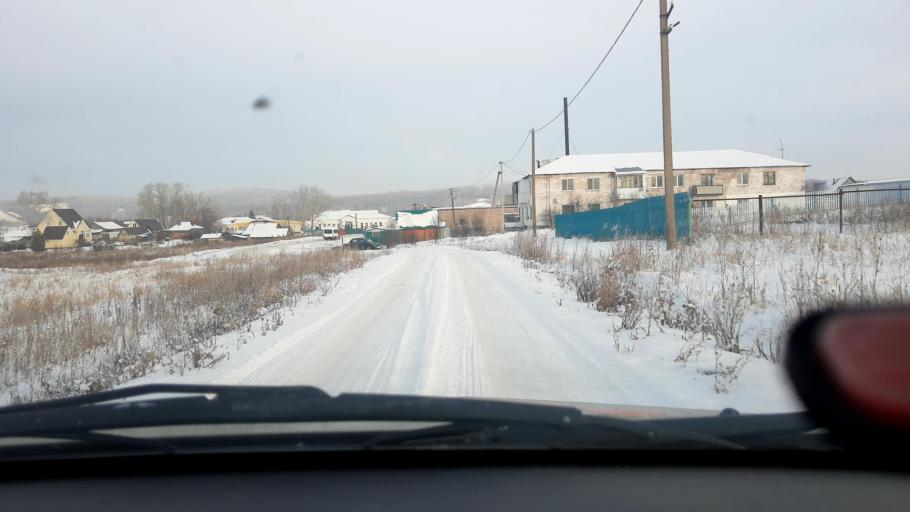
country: RU
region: Bashkortostan
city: Tolbazy
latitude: 54.3549
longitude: 55.8430
